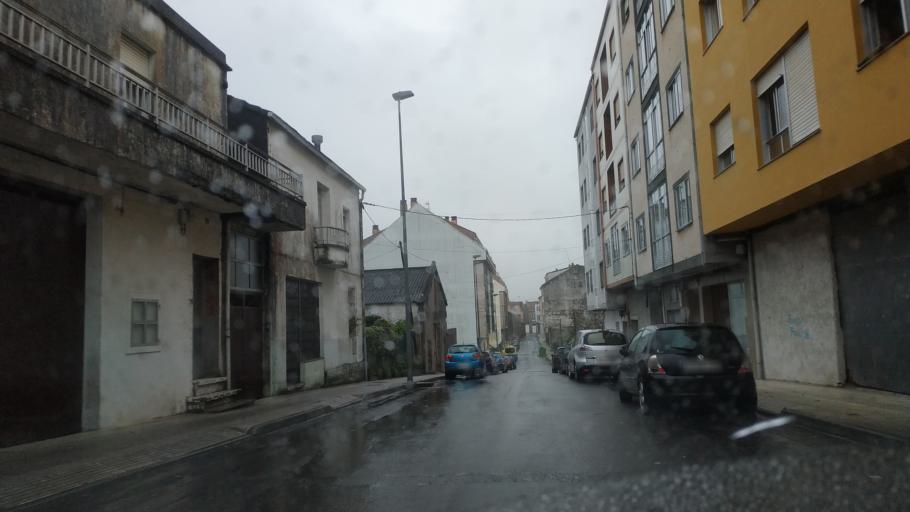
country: ES
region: Galicia
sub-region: Provincia da Coruna
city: Negreira
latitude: 42.9100
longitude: -8.7392
